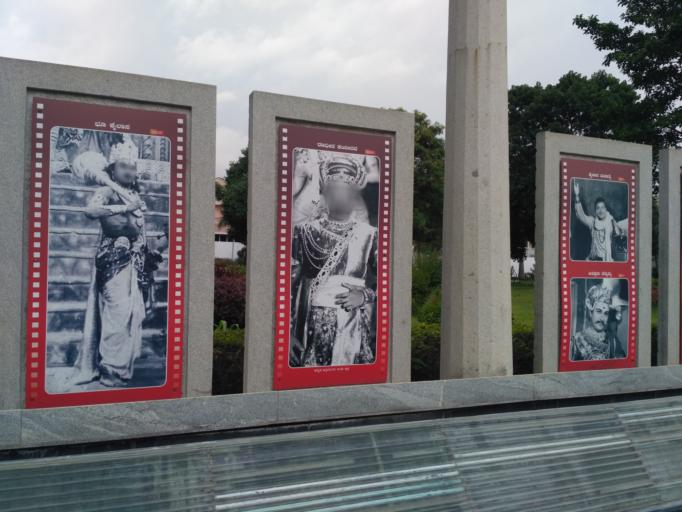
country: IN
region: Karnataka
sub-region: Bangalore Urban
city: Bangalore
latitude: 13.0187
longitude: 77.5324
